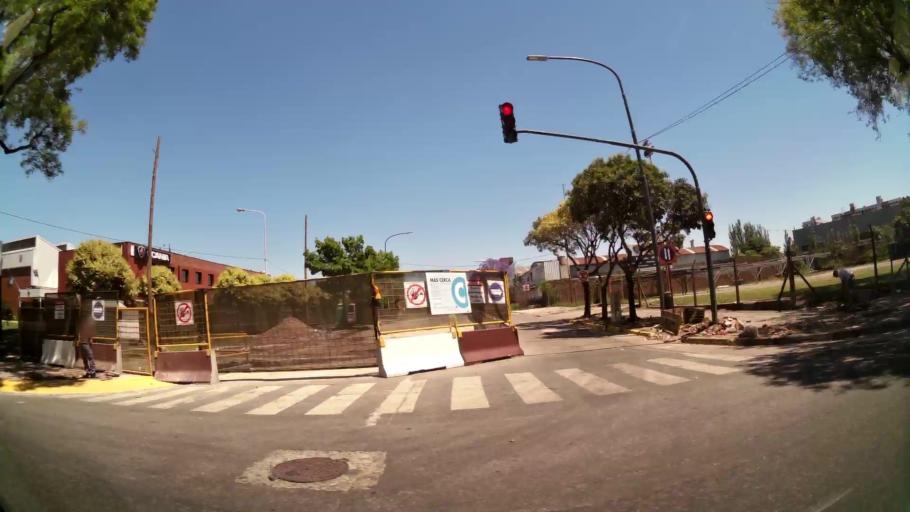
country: AR
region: Buenos Aires
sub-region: Partido de Avellaneda
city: Avellaneda
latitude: -34.6468
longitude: -58.3895
